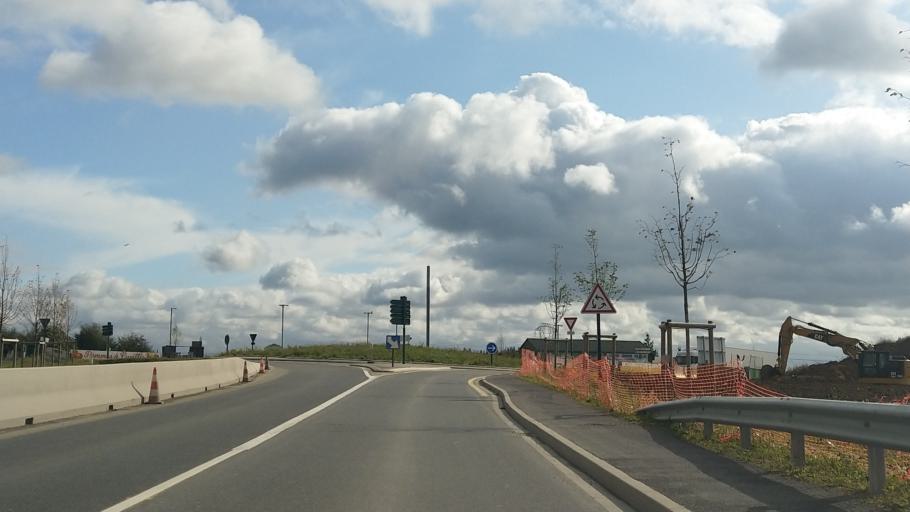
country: FR
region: Ile-de-France
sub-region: Departement du Val-d'Oise
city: Attainville
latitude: 49.0659
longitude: 2.3335
